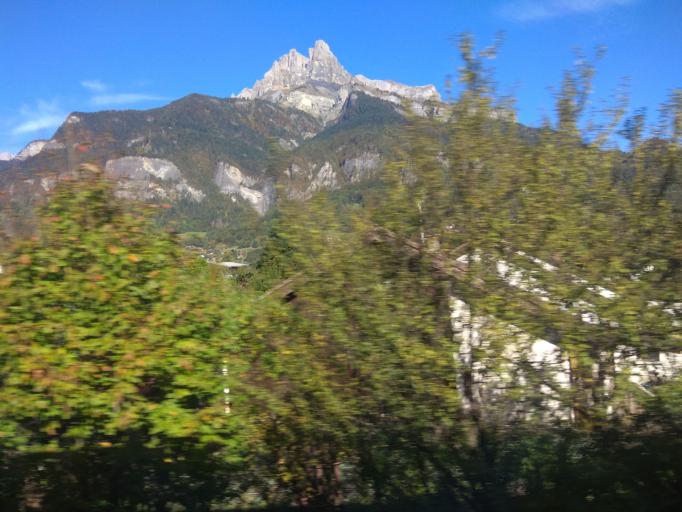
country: FR
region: Rhone-Alpes
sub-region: Departement de la Haute-Savoie
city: Sallanches
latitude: 45.9302
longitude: 6.6388
